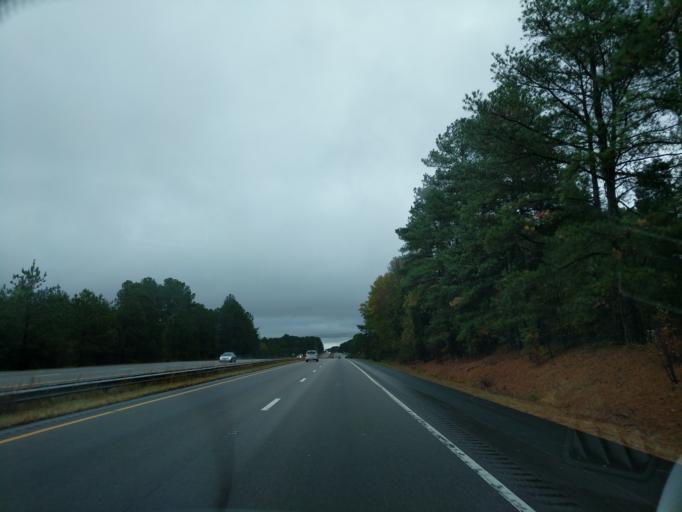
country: US
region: North Carolina
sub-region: Durham County
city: Gorman
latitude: 36.0546
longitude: -78.8007
